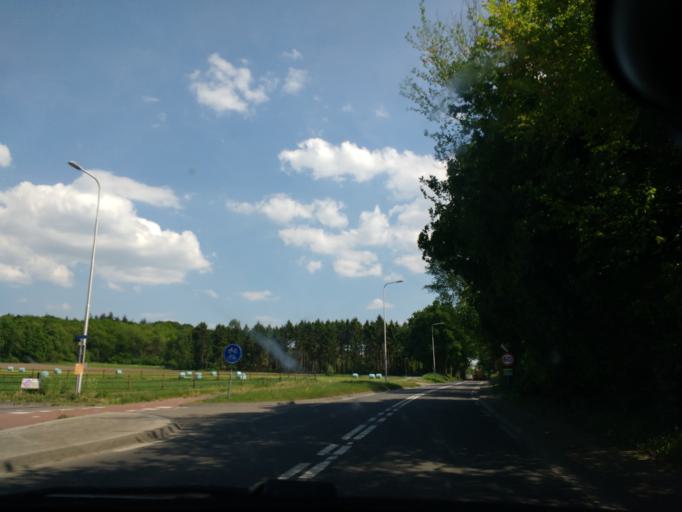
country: NL
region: Utrecht
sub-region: Gemeente Rhenen
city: Rhenen
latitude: 51.9664
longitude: 5.5462
